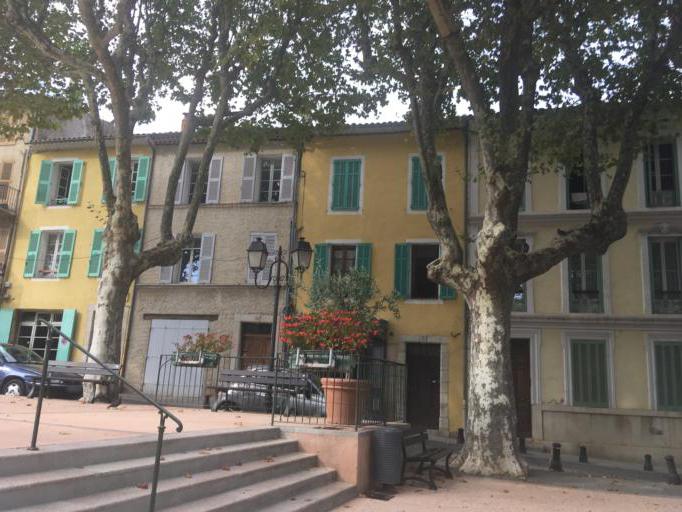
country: FR
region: Provence-Alpes-Cote d'Azur
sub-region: Departement du Var
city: Lorgues
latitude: 43.4933
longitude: 6.3576
